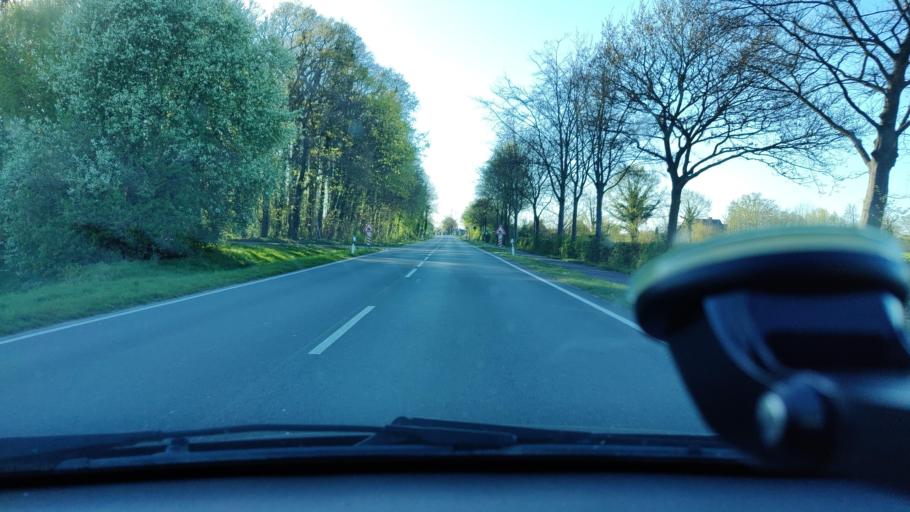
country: DE
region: North Rhine-Westphalia
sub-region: Regierungsbezirk Munster
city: Ahaus
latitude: 52.0635
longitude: 7.0279
